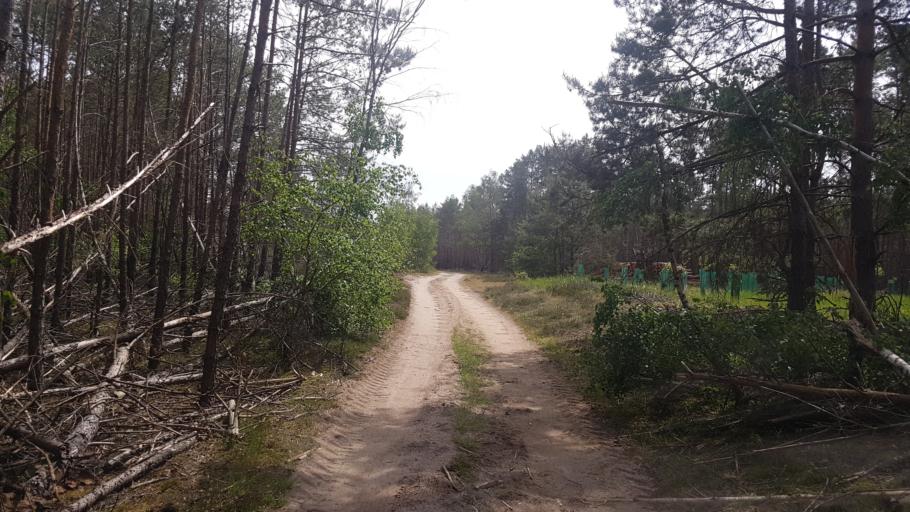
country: DE
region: Brandenburg
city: Doberlug-Kirchhain
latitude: 51.6155
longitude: 13.6214
